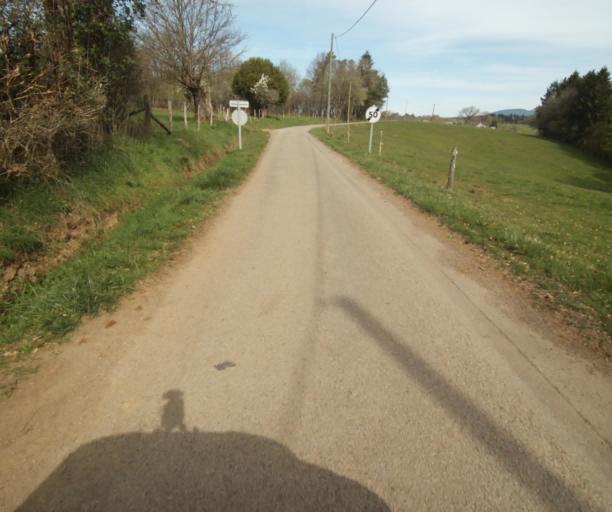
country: FR
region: Limousin
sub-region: Departement de la Correze
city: Correze
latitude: 45.3708
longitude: 1.8199
